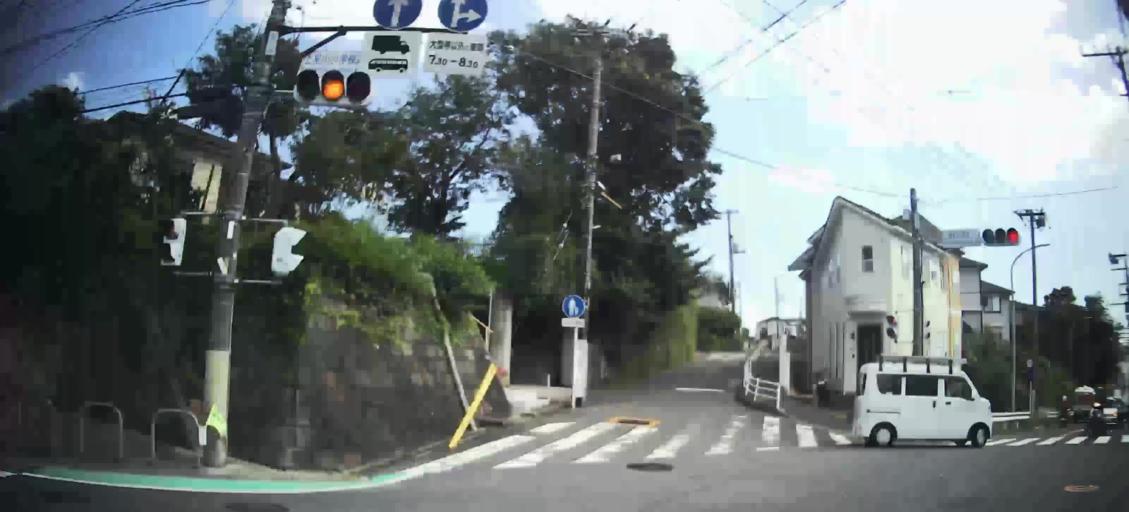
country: JP
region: Kanagawa
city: Yokohama
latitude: 35.4807
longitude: 139.5771
